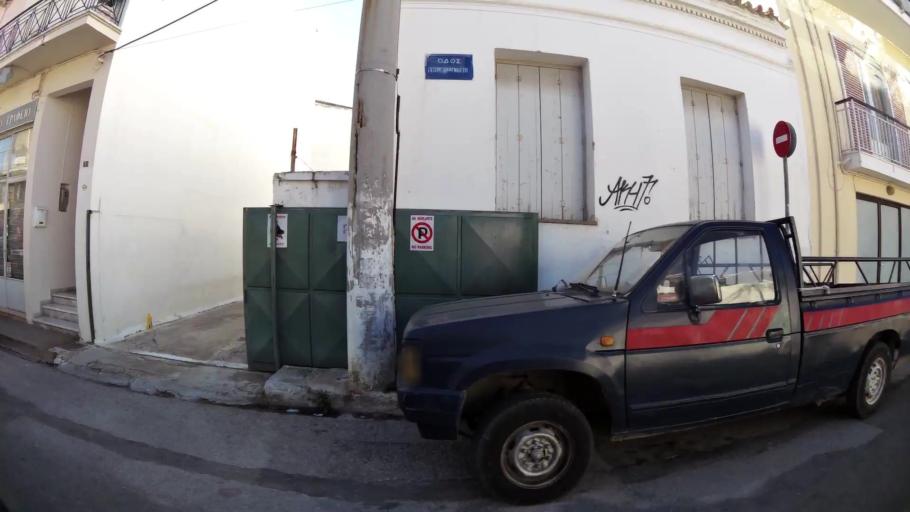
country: GR
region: Attica
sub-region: Nomarchia Anatolikis Attikis
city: Koropi
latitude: 37.8995
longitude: 23.8706
